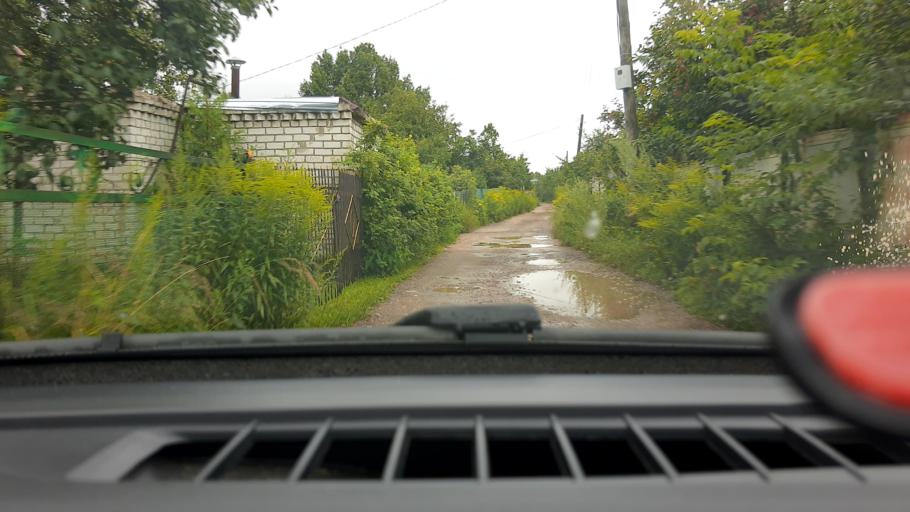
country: RU
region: Nizjnij Novgorod
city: Gorbatovka
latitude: 56.3169
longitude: 43.8362
